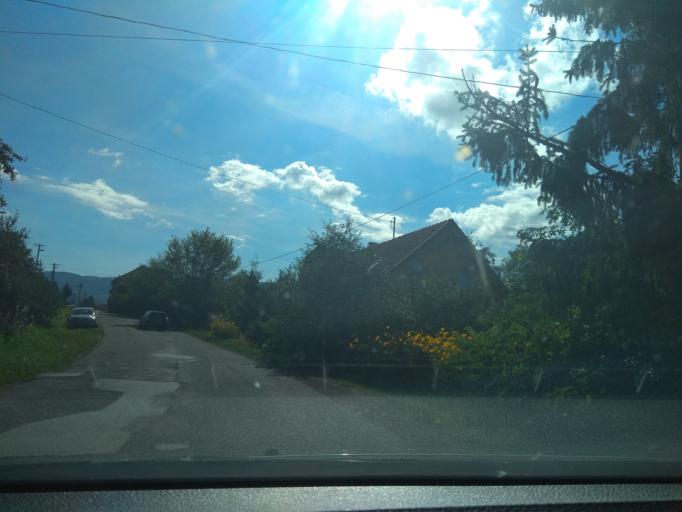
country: HU
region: Heves
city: Belapatfalva
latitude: 48.0562
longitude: 20.3217
